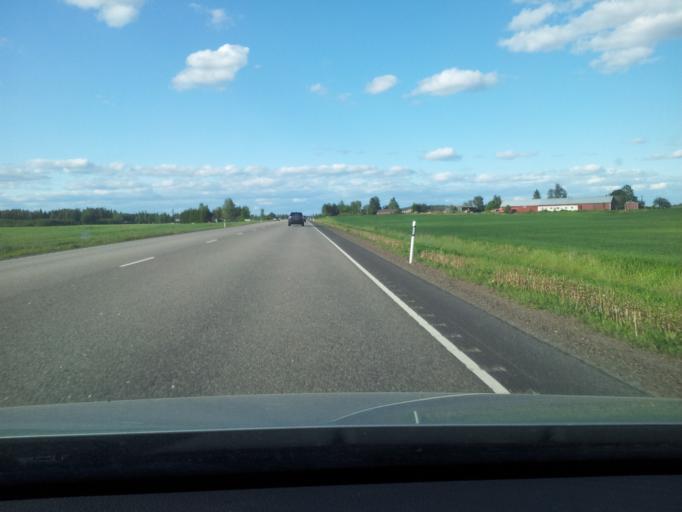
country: FI
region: Kymenlaakso
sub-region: Kouvola
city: Elimaeki
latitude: 60.7498
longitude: 26.4552
